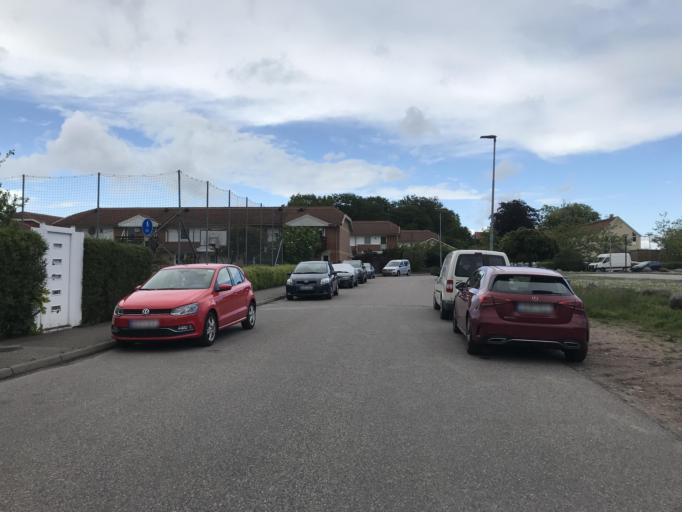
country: SE
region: Skane
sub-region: Malmo
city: Malmoe
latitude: 55.5685
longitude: 13.0406
